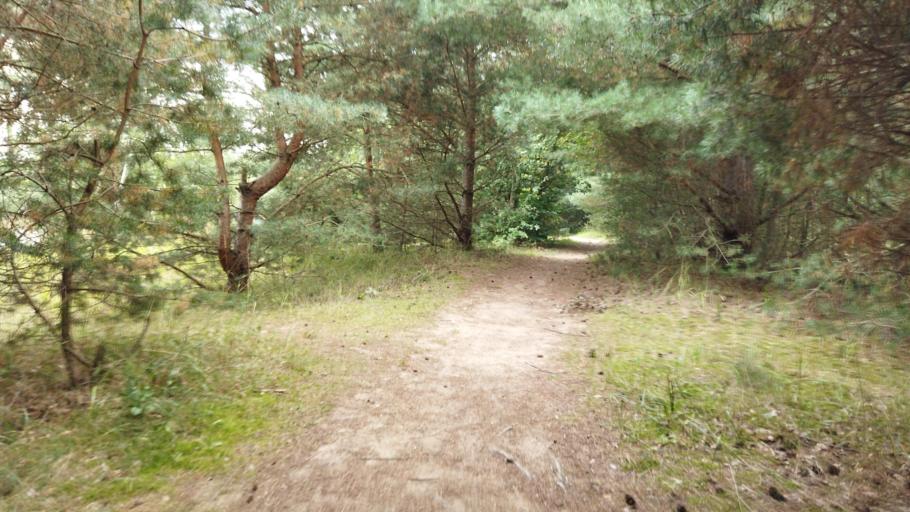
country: DE
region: Lower Saxony
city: Glandorf
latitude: 52.0990
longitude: 8.0421
